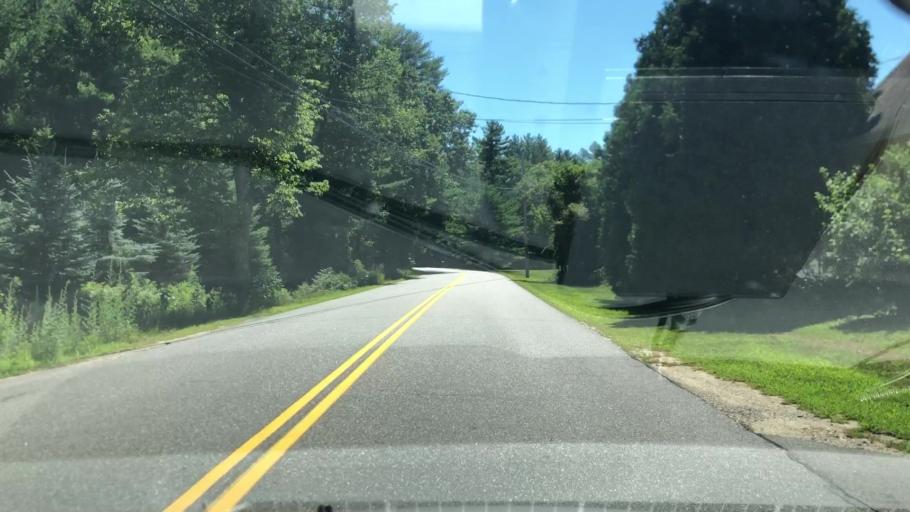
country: US
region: New Hampshire
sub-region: Hillsborough County
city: Milford
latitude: 42.8586
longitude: -71.5917
